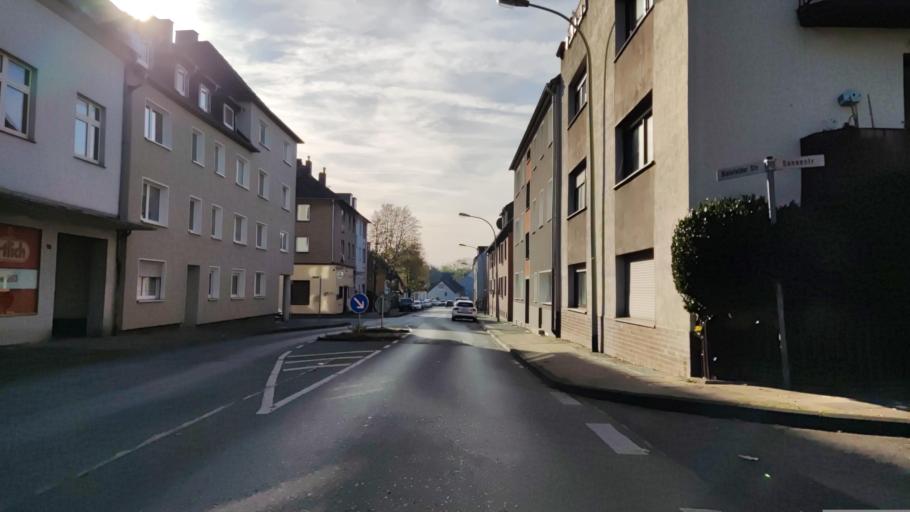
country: DE
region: North Rhine-Westphalia
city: Bochum-Hordel
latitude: 51.5259
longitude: 7.1837
